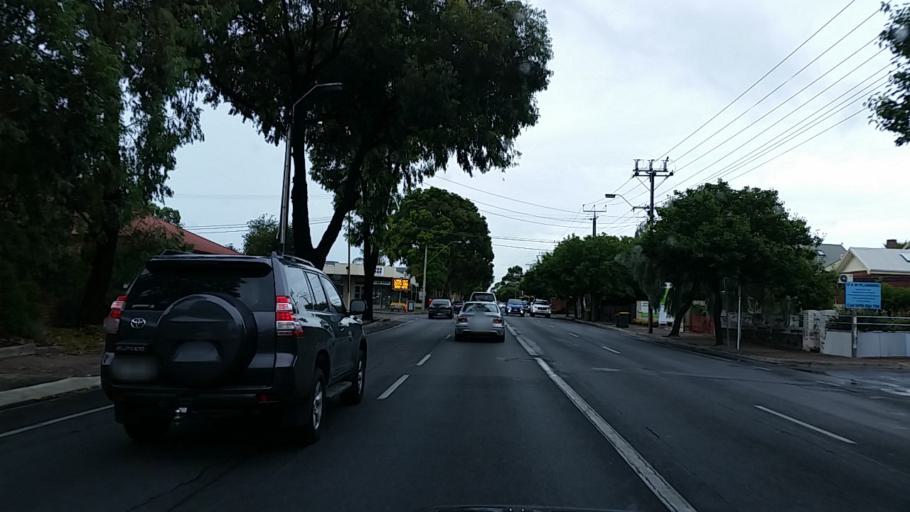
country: AU
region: South Australia
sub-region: Norwood Payneham St Peters
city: Royston Park
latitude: -34.9066
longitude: 138.6303
